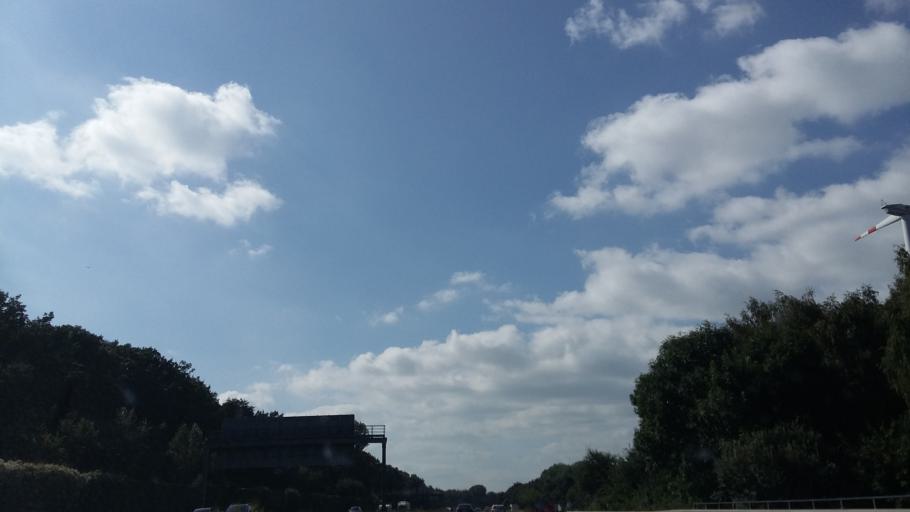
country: DE
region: Bremen
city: Bremen
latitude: 53.1196
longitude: 8.7957
